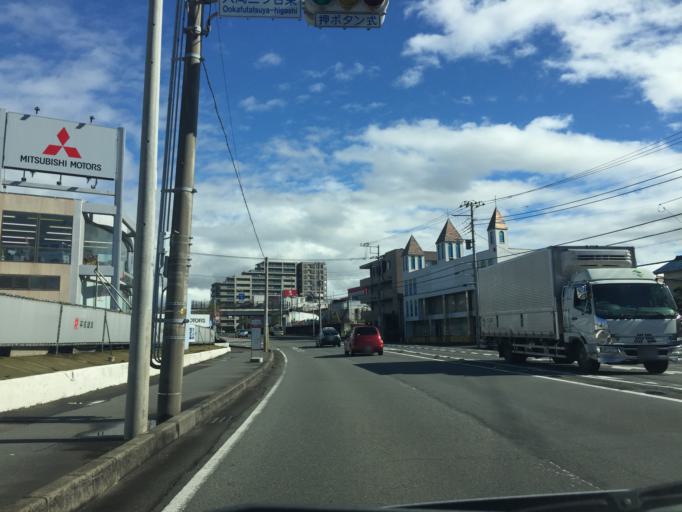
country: JP
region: Shizuoka
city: Numazu
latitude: 35.1006
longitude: 138.8741
